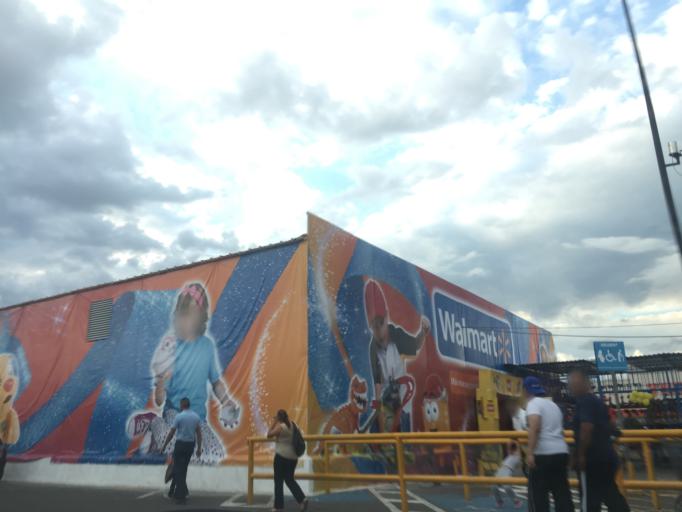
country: MX
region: Guanajuato
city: Leon
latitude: 21.1619
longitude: -101.6915
